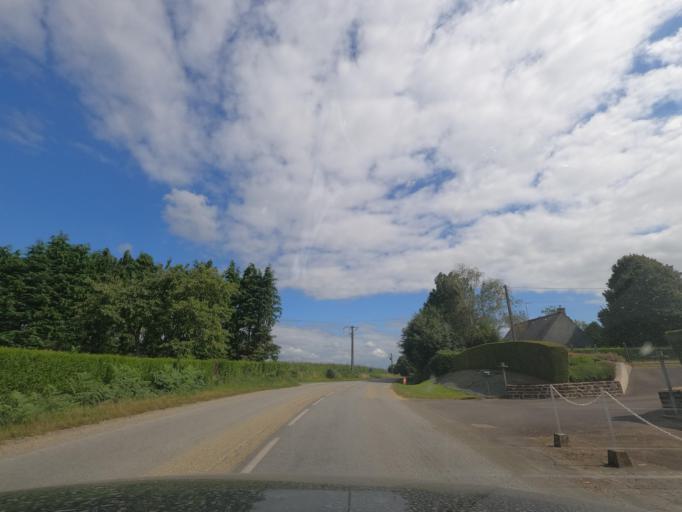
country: FR
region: Pays de la Loire
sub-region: Departement de la Mayenne
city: Landivy
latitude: 48.4789
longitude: -1.0203
